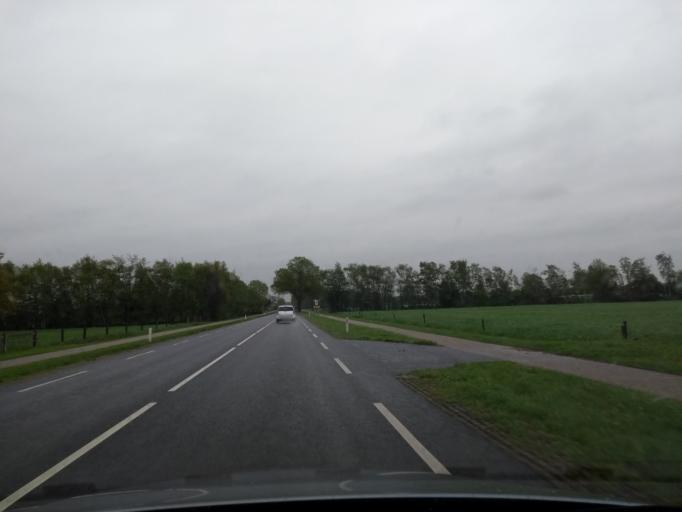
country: NL
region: Overijssel
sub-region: Gemeente Tubbergen
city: Tubbergen
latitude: 52.3831
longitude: 6.8157
